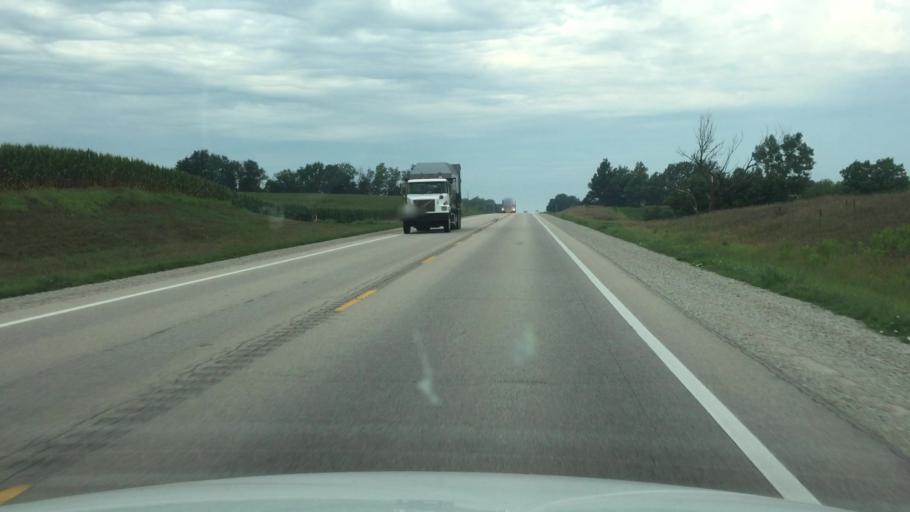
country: US
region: Kansas
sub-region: Brown County
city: Hiawatha
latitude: 39.8486
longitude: -95.6079
